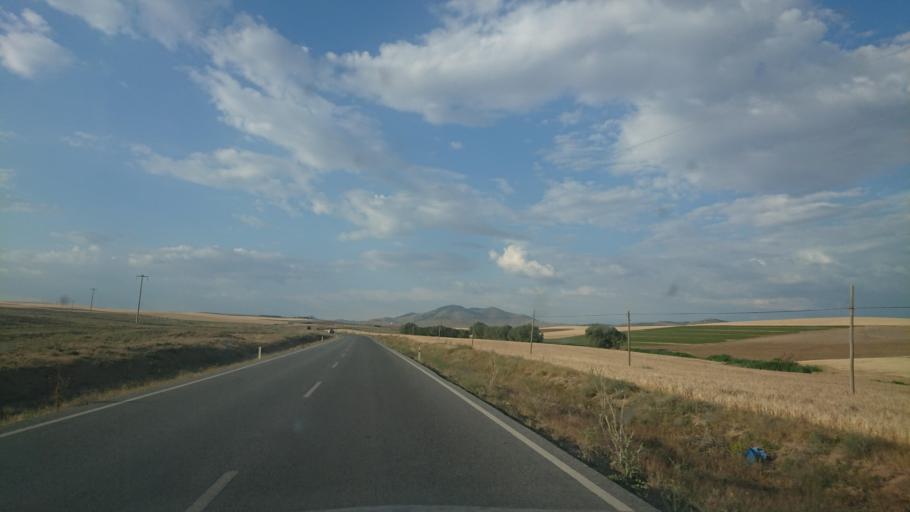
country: TR
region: Aksaray
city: Aksaray
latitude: 38.4824
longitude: 34.0651
